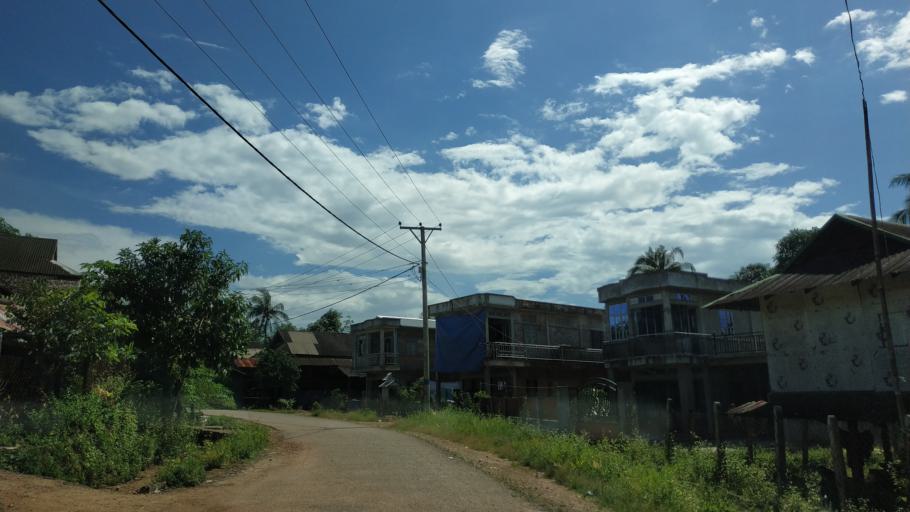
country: MM
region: Tanintharyi
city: Dawei
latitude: 14.2149
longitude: 98.1925
